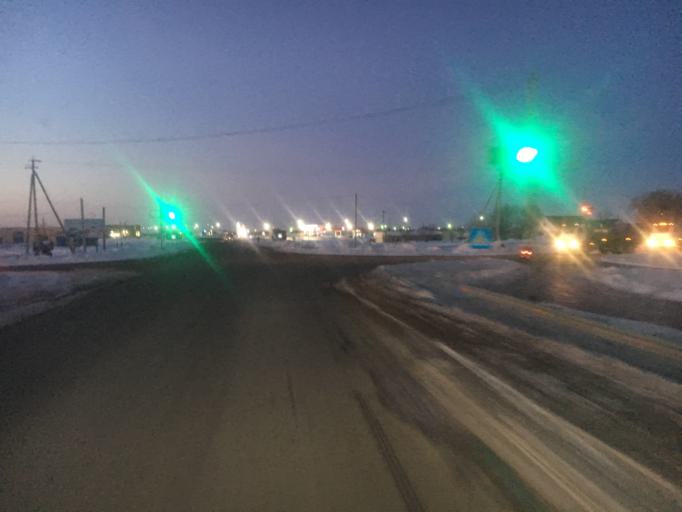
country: KZ
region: Batys Qazaqstan
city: Oral
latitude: 51.1536
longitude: 51.4890
